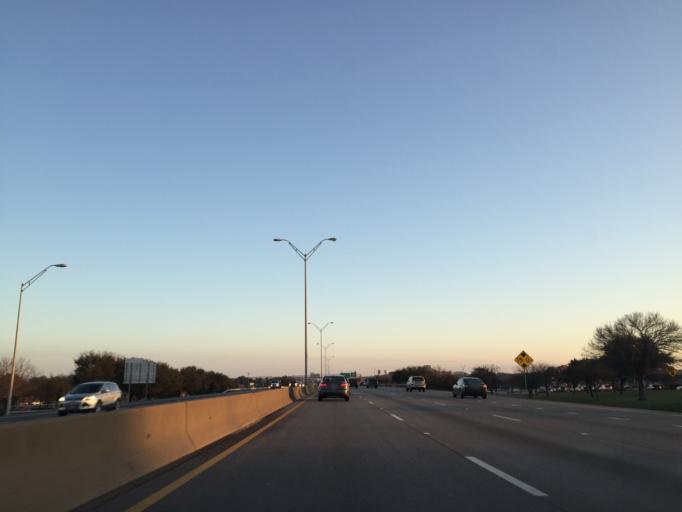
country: US
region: Texas
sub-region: Williamson County
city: Round Rock
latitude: 30.5198
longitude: -97.6887
